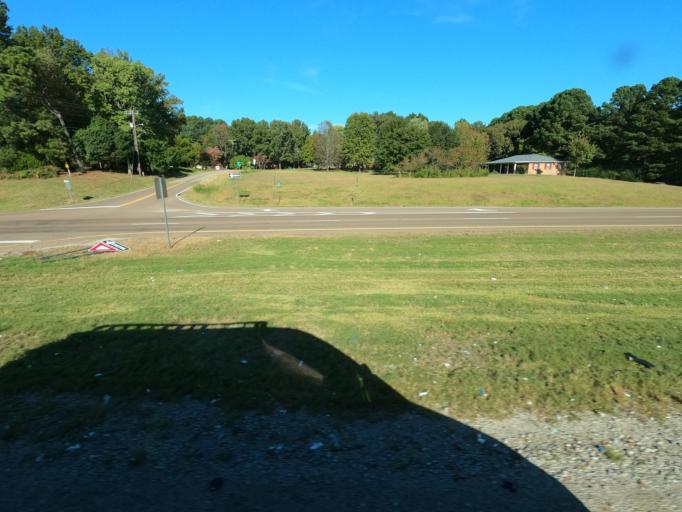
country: US
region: Tennessee
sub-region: Tipton County
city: Munford
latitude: 35.4171
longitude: -89.8244
